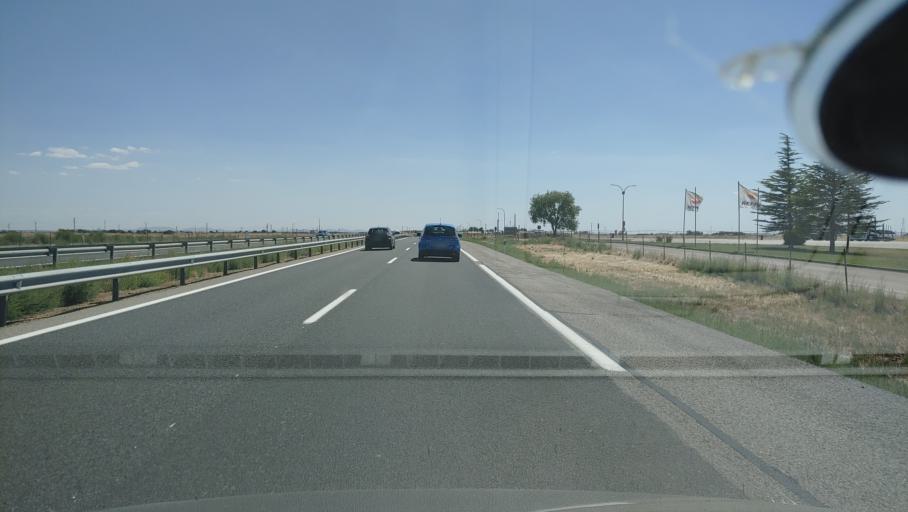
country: ES
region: Castille-La Mancha
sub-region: Provincia de Ciudad Real
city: Villarta de San Juan
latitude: 39.1812
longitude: -3.3985
